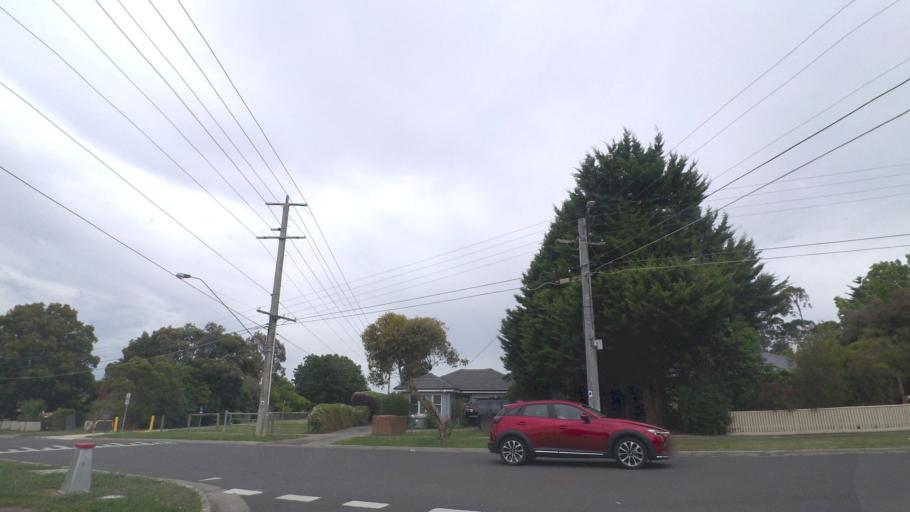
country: AU
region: Victoria
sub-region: Yarra Ranges
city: Kilsyth
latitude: -37.7993
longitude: 145.3045
